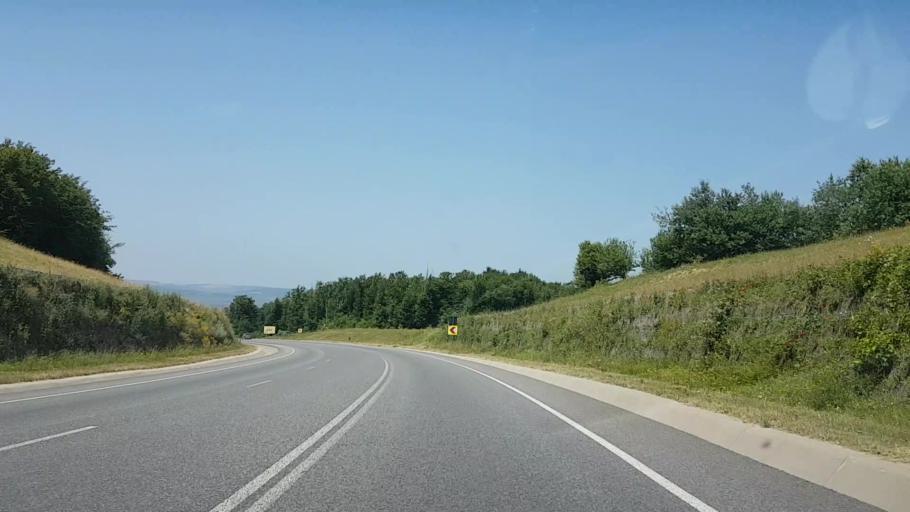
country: RO
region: Cluj
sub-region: Comuna Feleacu
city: Gheorghieni
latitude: 46.7150
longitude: 23.6627
